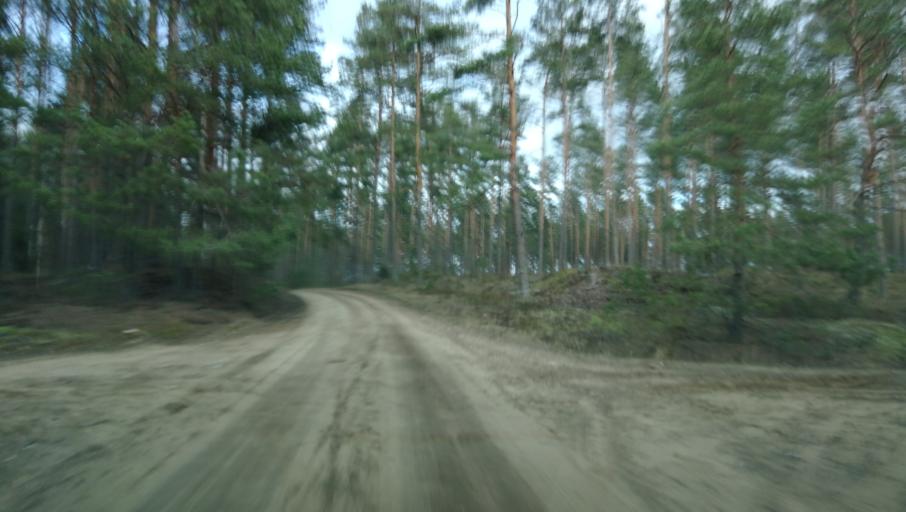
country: LV
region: Adazi
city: Adazi
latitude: 57.0618
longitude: 24.2623
